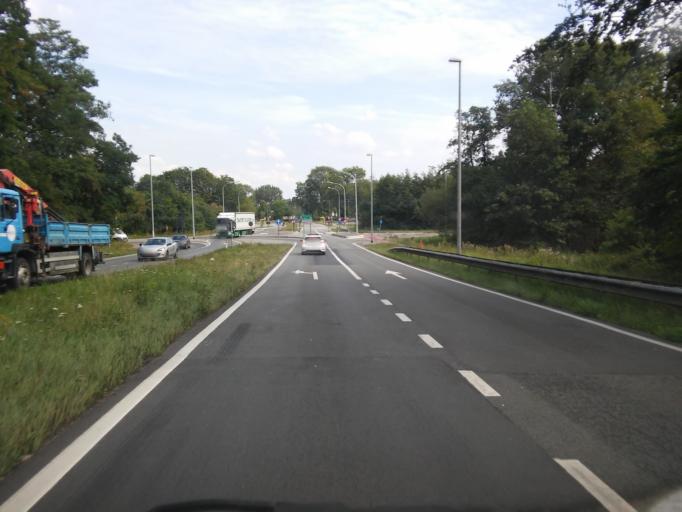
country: BE
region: Flanders
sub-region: Provincie Antwerpen
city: Willebroek
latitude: 51.0596
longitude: 4.3417
